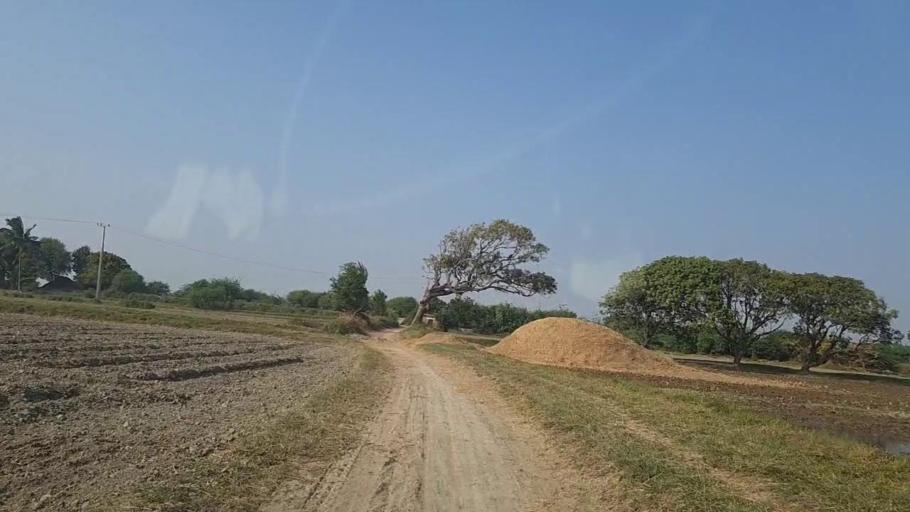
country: PK
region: Sindh
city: Mirpur Sakro
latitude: 24.5728
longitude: 67.6843
